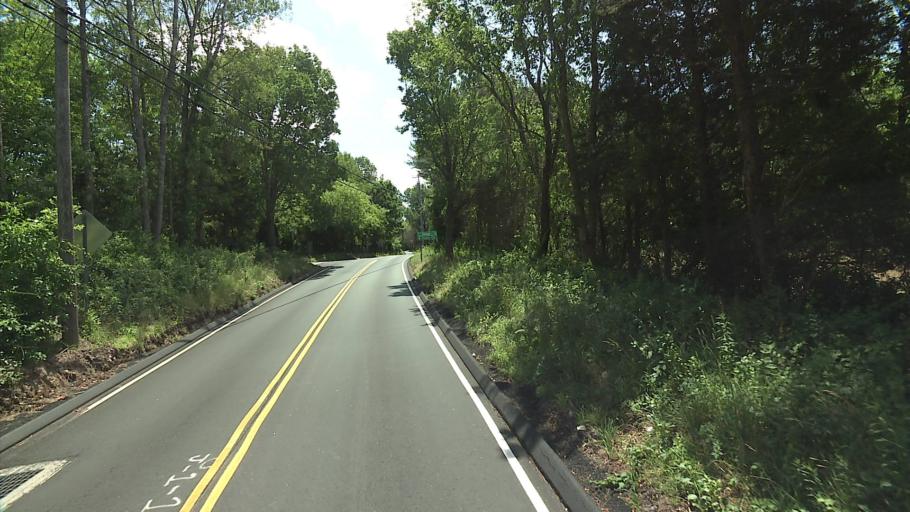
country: US
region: Connecticut
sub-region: New London County
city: Jewett City
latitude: 41.5809
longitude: -71.8990
